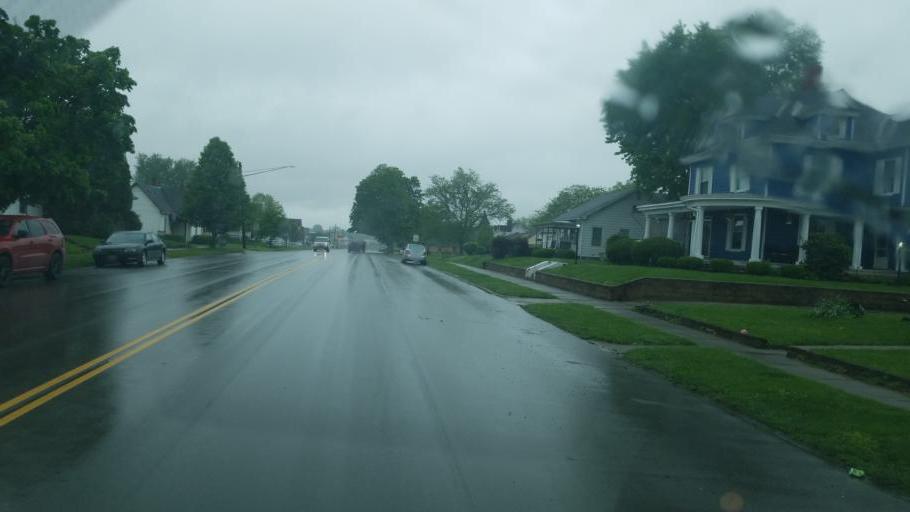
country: US
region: Ohio
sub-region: Highland County
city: Greenfield
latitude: 39.3493
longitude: -83.3937
